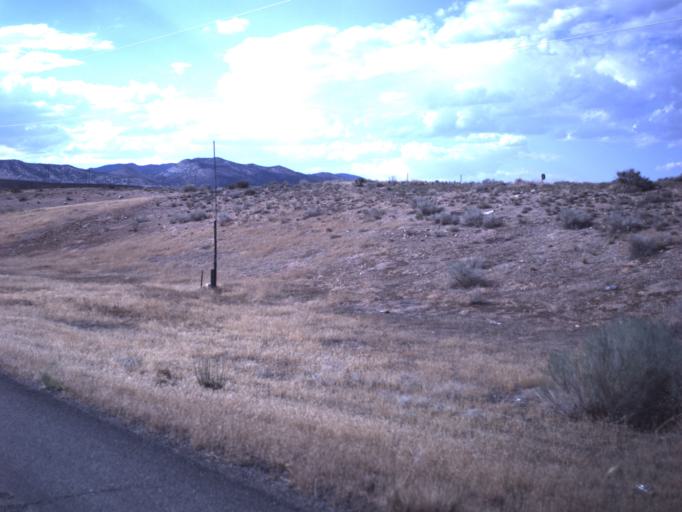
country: US
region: Utah
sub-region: Sevier County
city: Aurora
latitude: 38.9593
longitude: -111.9256
